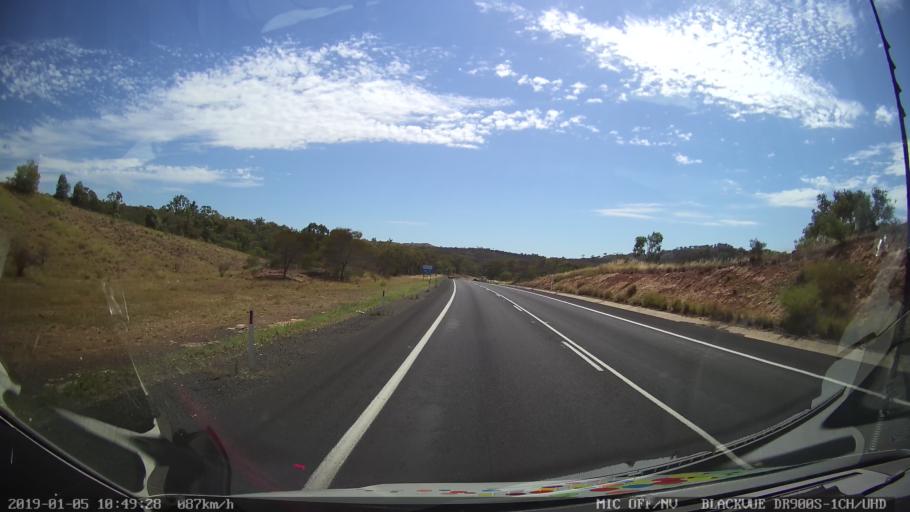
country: AU
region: New South Wales
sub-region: Warrumbungle Shire
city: Coonabarabran
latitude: -31.4340
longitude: 149.0614
